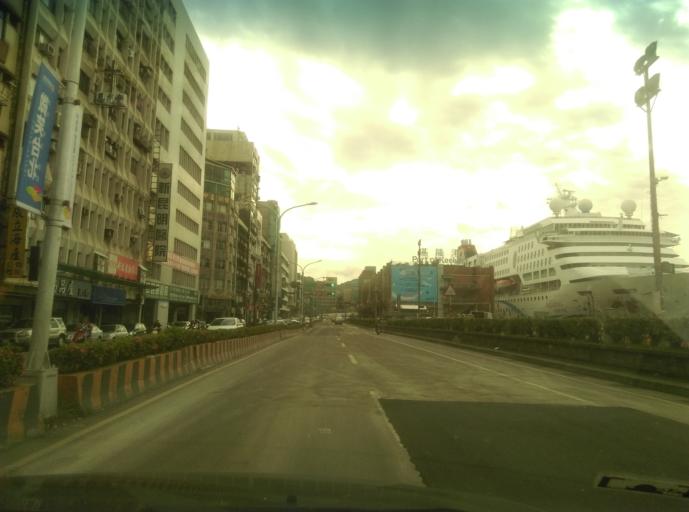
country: TW
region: Taiwan
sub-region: Keelung
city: Keelung
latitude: 25.1339
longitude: 121.7451
